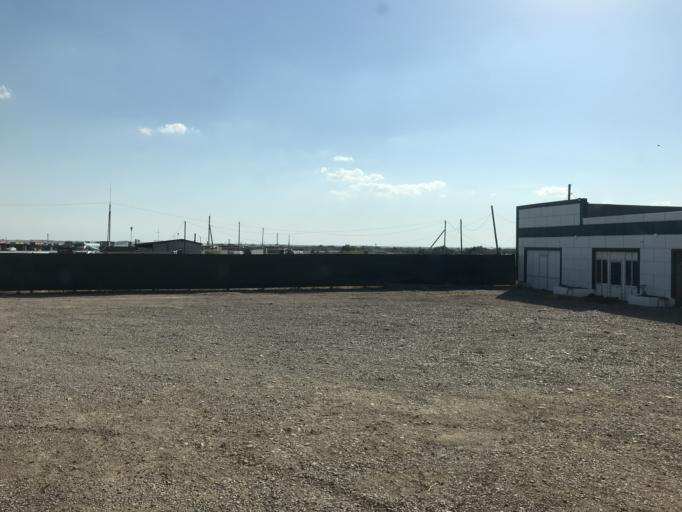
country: KG
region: Chuy
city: Sokuluk
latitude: 43.2701
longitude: 74.2238
